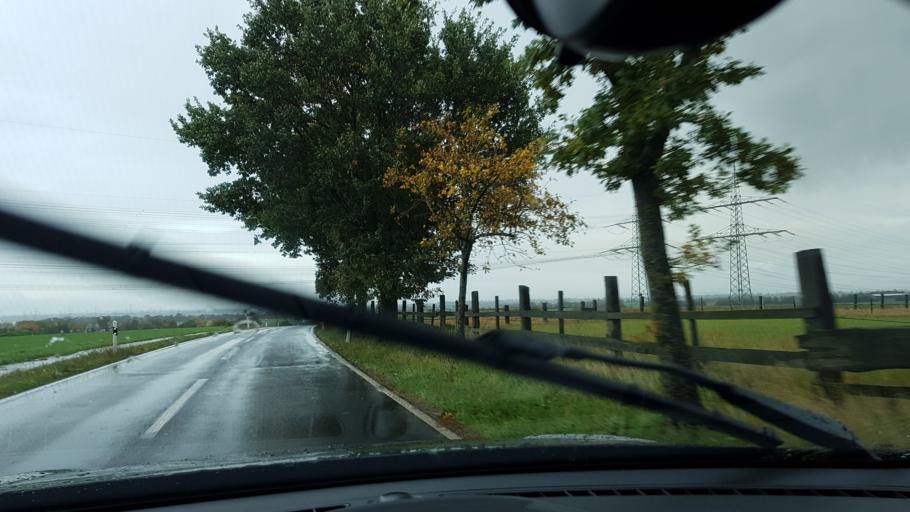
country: DE
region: North Rhine-Westphalia
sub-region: Regierungsbezirk Dusseldorf
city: Rommerskirchen
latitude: 51.0486
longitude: 6.6313
